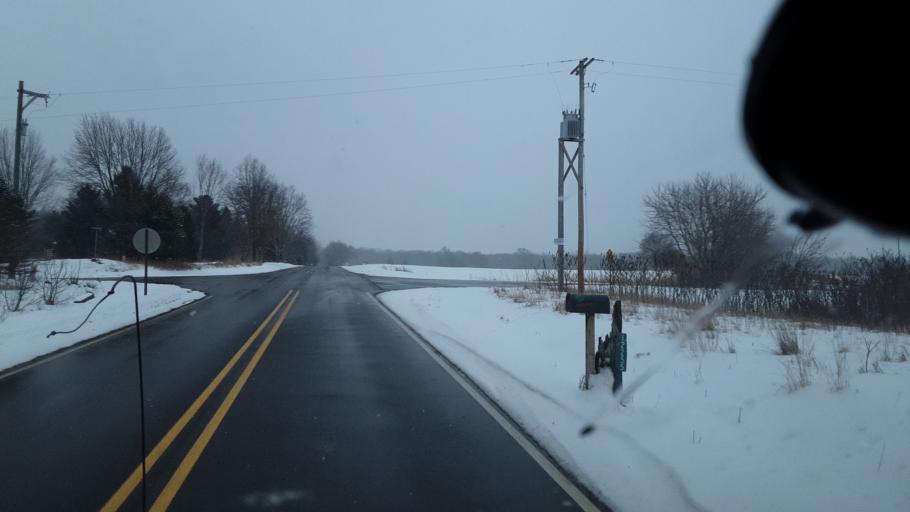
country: US
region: Michigan
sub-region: Ingham County
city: Leslie
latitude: 42.4121
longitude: -84.4434
